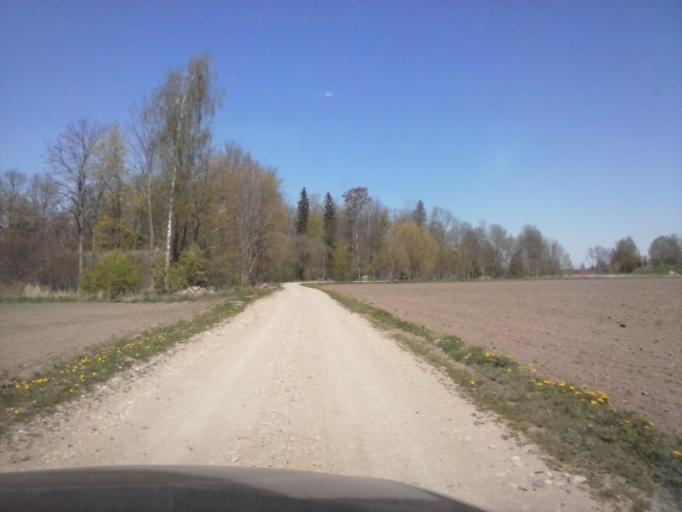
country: EE
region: Valgamaa
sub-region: Torva linn
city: Torva
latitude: 58.2324
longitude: 25.9003
